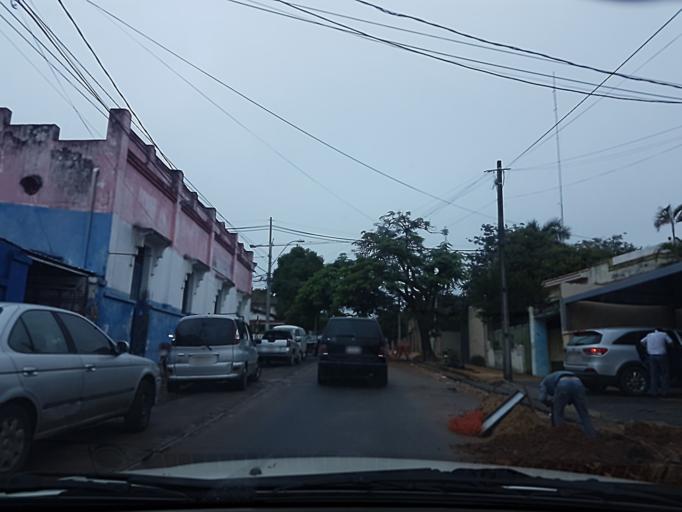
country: PY
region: Asuncion
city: Asuncion
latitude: -25.2833
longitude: -57.6123
